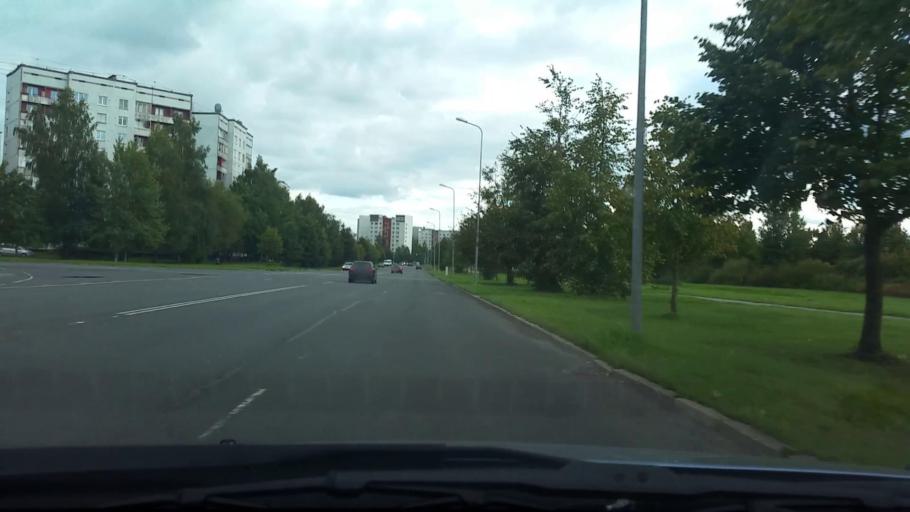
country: LV
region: Stopini
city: Ulbroka
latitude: 56.9689
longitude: 24.2312
